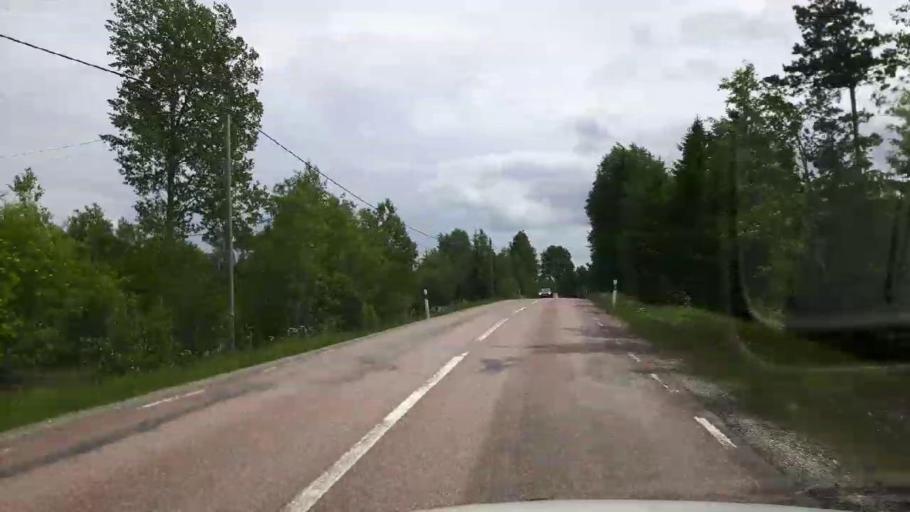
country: SE
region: Vaestmanland
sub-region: Fagersta Kommun
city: Fagersta
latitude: 59.9365
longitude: 15.8205
